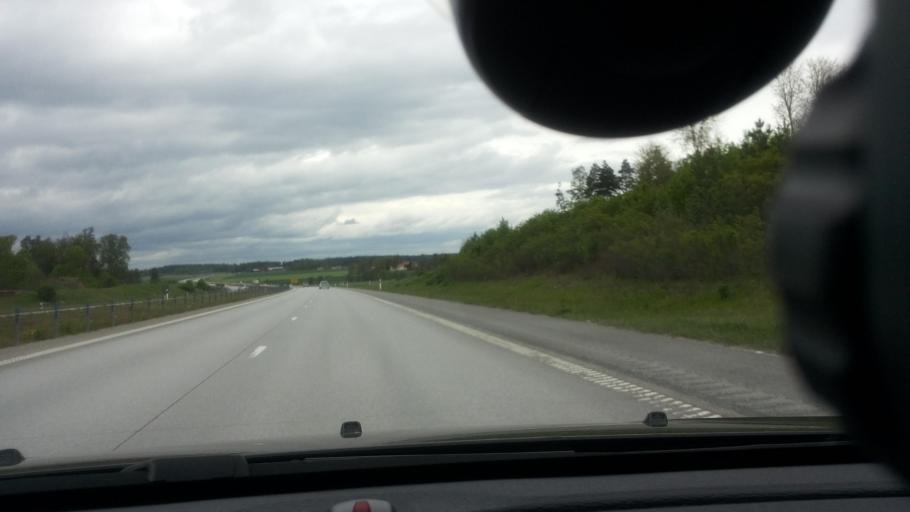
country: SE
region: Uppsala
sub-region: Uppsala Kommun
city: Storvreta
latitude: 59.9412
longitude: 17.6599
